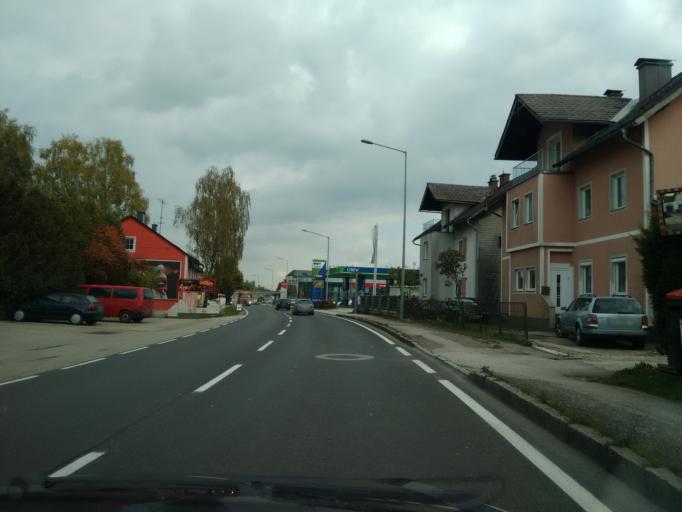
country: AT
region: Upper Austria
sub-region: Politischer Bezirk Vocklabruck
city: Attnang-Puchheim
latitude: 48.0054
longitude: 13.7083
